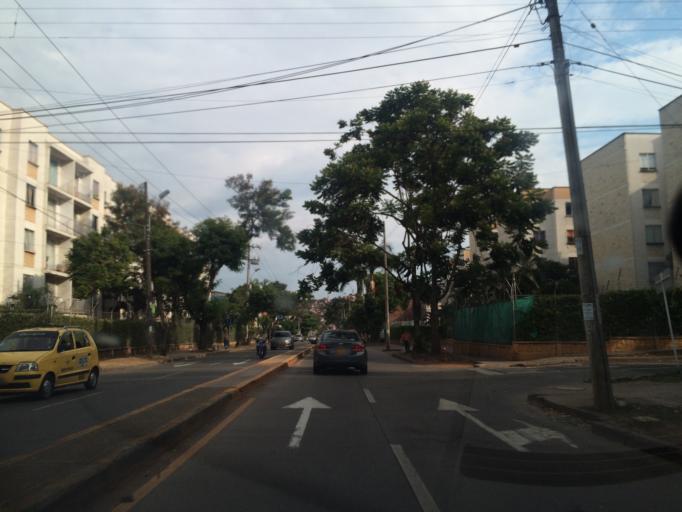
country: CO
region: Valle del Cauca
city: Cali
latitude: 3.3952
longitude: -76.5571
